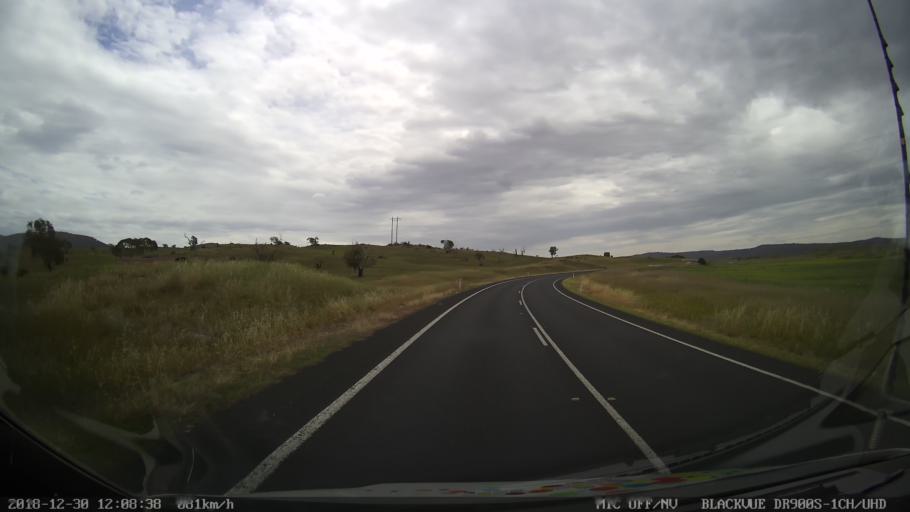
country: AU
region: New South Wales
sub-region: Snowy River
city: Jindabyne
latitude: -36.3928
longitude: 148.5942
